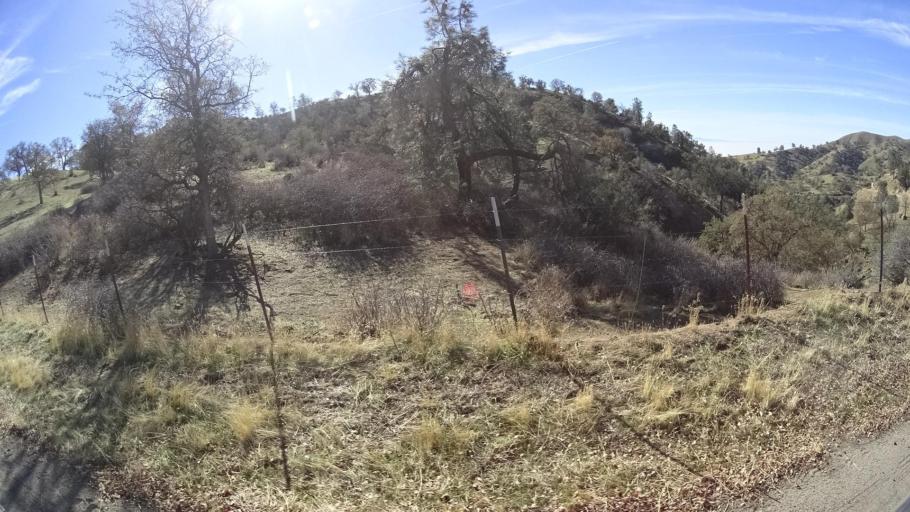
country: US
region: California
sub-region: Kern County
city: Arvin
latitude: 35.4413
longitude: -118.7223
